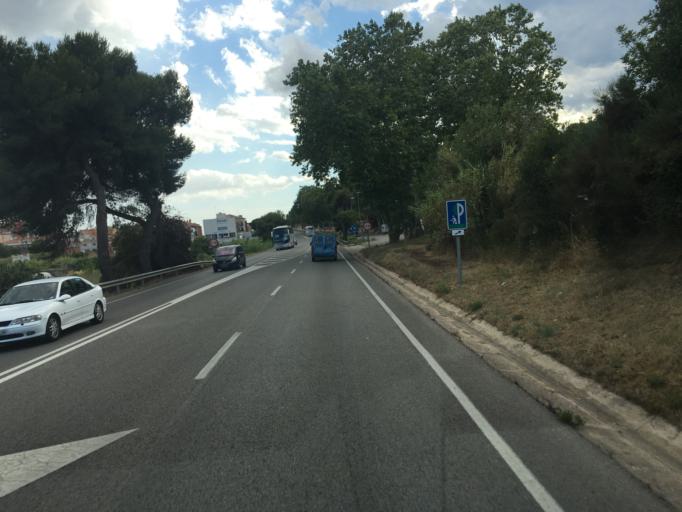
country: ES
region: Catalonia
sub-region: Provincia de Barcelona
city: Malgrat de Mar
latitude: 41.6476
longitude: 2.7330
